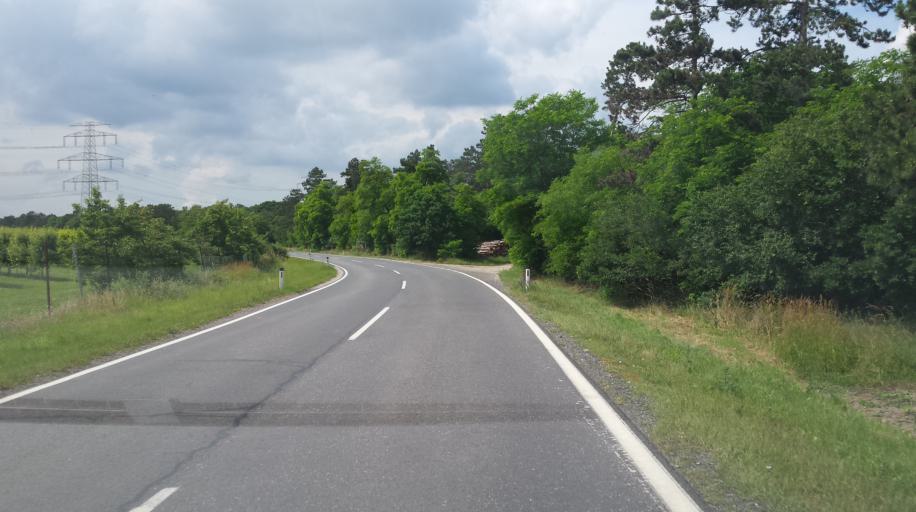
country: AT
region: Lower Austria
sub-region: Politischer Bezirk Ganserndorf
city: Deutsch-Wagram
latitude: 48.3035
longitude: 16.5443
